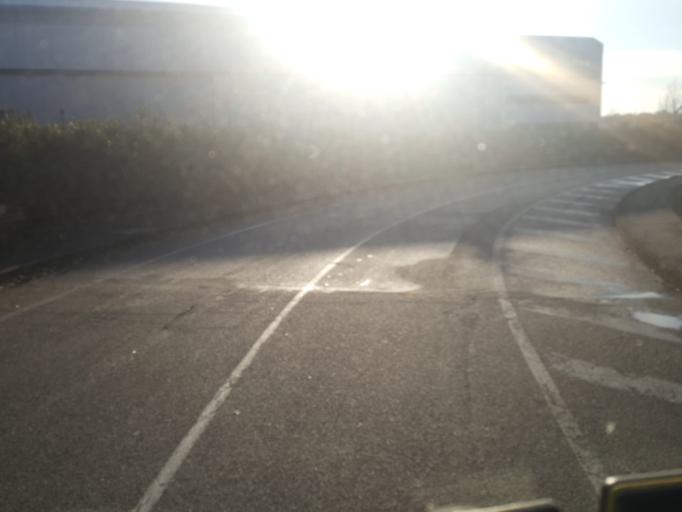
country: IT
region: Friuli Venezia Giulia
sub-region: Provincia di Gorizia
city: Monfalcone
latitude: 45.7963
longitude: 13.5743
